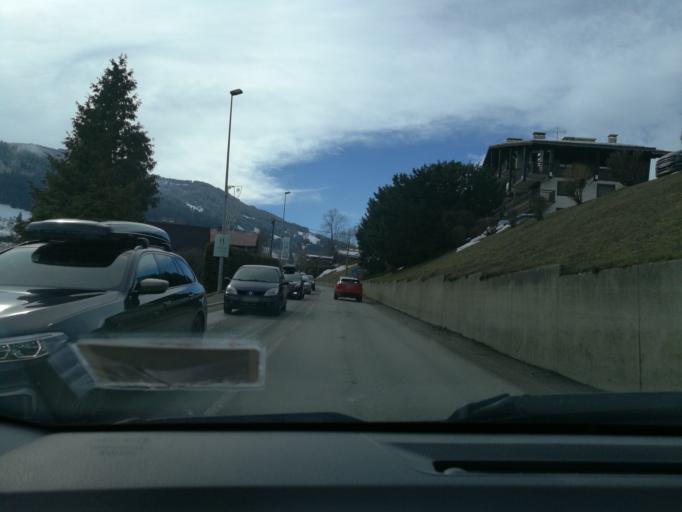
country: FR
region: Rhone-Alpes
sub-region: Departement de la Haute-Savoie
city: Combloux
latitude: 45.8924
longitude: 6.6451
